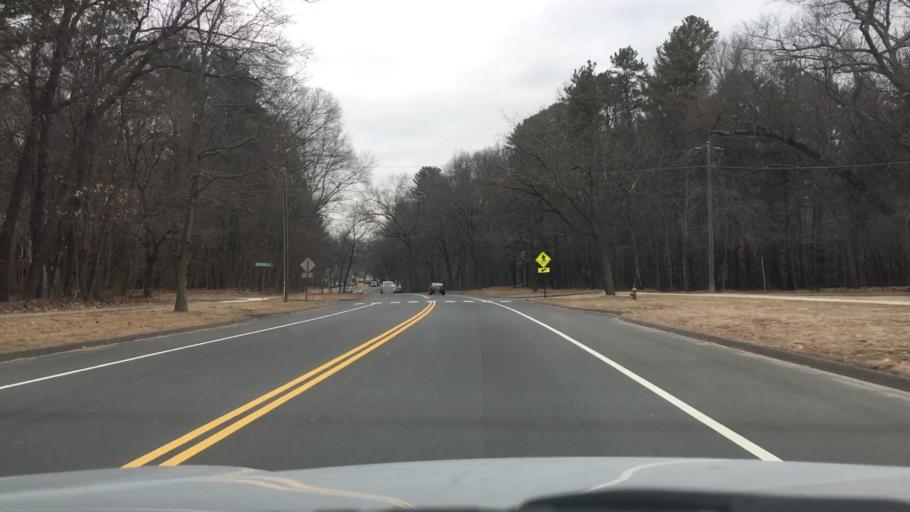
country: US
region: Massachusetts
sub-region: Hampden County
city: Longmeadow
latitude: 42.0580
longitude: -72.5720
